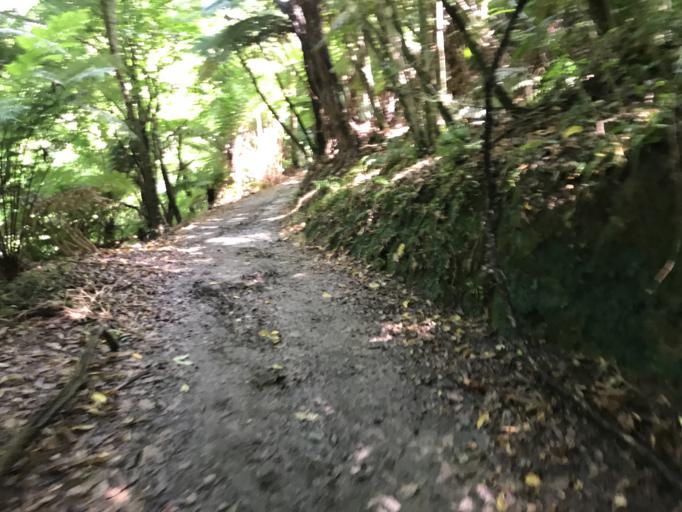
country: NZ
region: Marlborough
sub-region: Marlborough District
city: Picton
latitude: -41.2587
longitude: 173.9339
